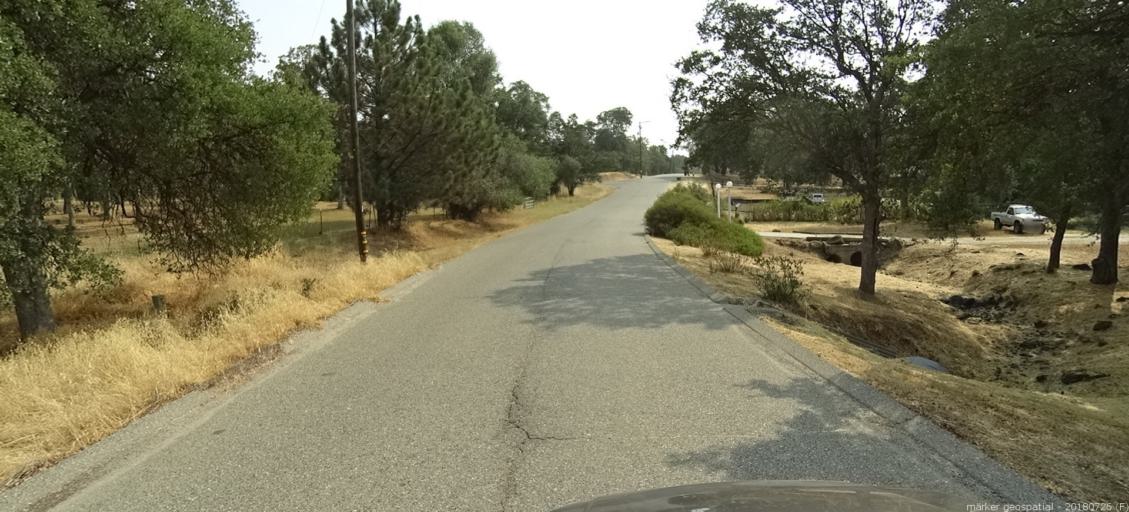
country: US
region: California
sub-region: Madera County
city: Coarsegold
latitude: 37.2159
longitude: -119.6859
